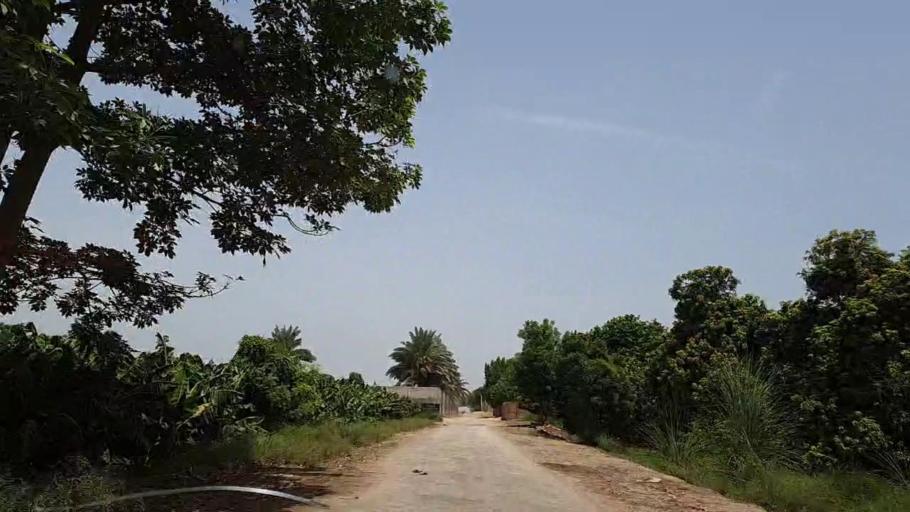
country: PK
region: Sindh
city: Tharu Shah
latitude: 26.9495
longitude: 68.0256
